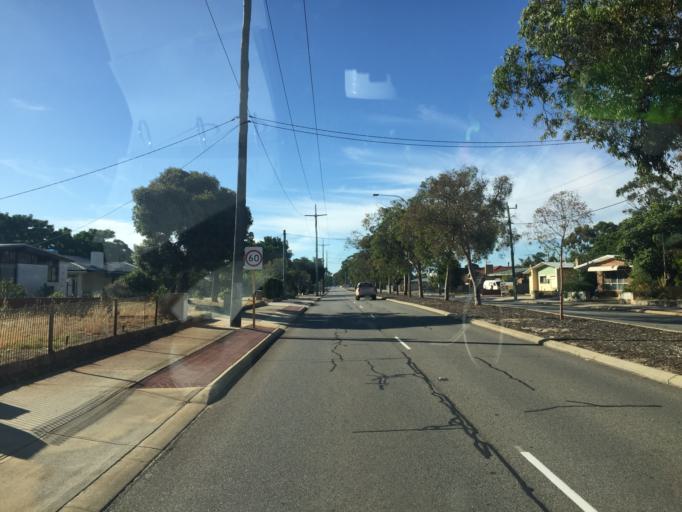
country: AU
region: Western Australia
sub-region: Belmont
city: Kewdale
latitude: -31.9678
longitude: 115.9424
